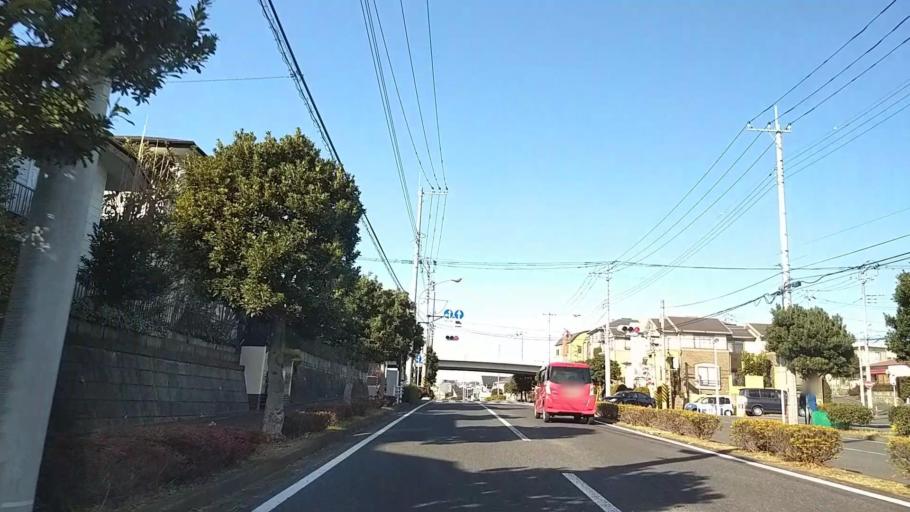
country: JP
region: Kanagawa
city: Atsugi
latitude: 35.4391
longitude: 139.3296
